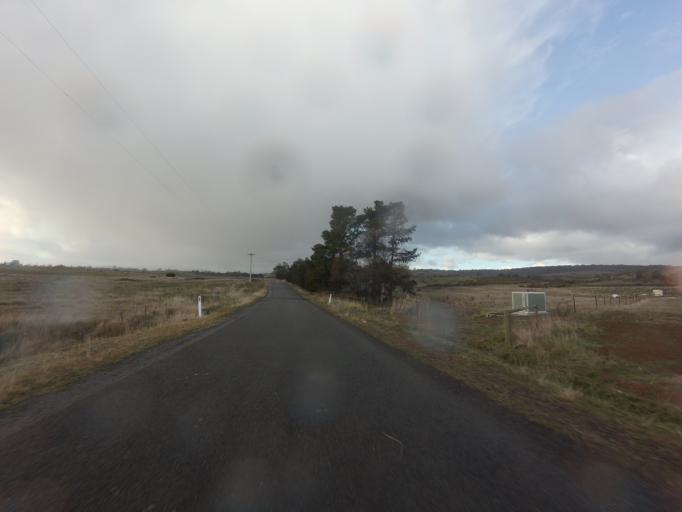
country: AU
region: Tasmania
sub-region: Break O'Day
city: St Helens
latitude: -42.0034
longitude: 148.0847
